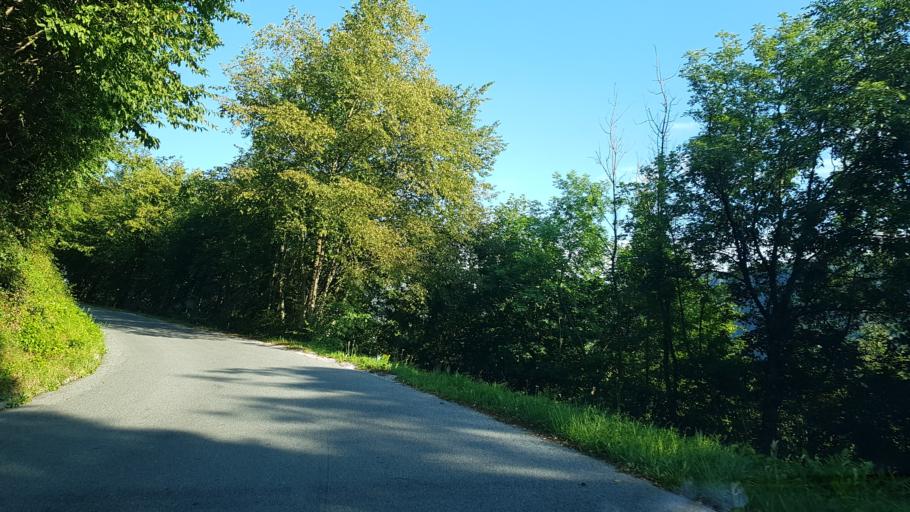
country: SI
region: Cerkno
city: Cerkno
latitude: 46.0816
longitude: 13.9849
